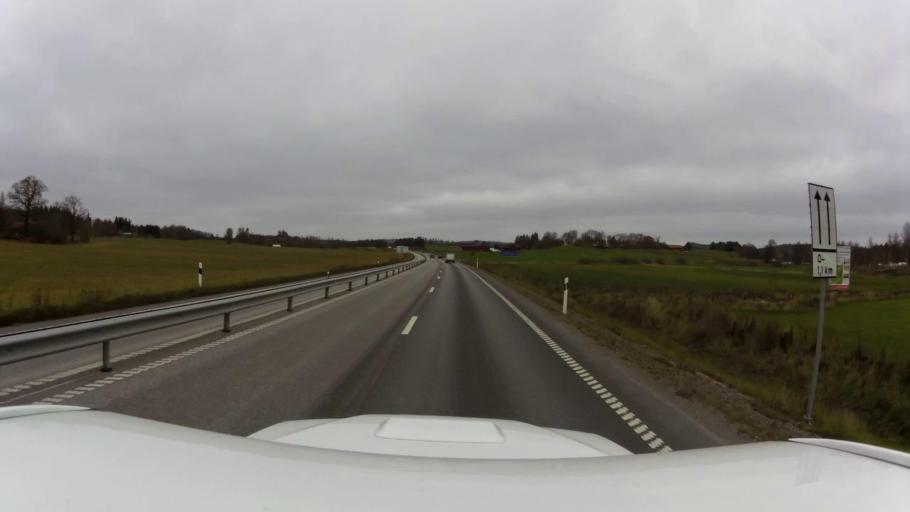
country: SE
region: OEstergoetland
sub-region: Kinda Kommun
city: Rimforsa
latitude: 58.1403
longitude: 15.6810
